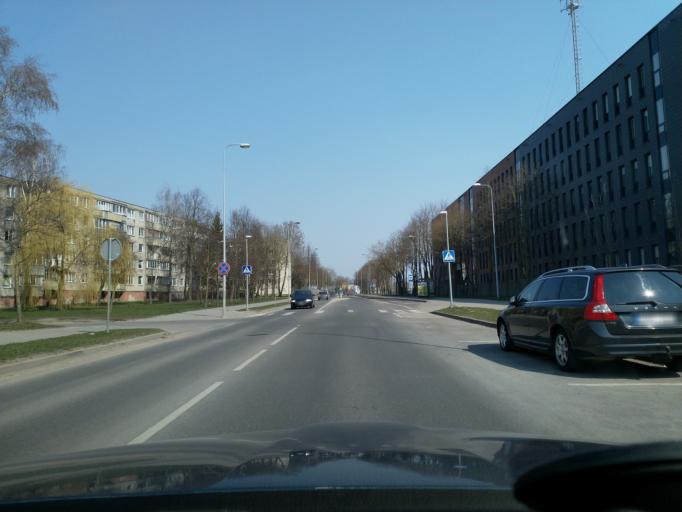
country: LT
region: Klaipedos apskritis
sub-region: Klaipeda
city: Klaipeda
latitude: 55.6974
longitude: 21.1609
